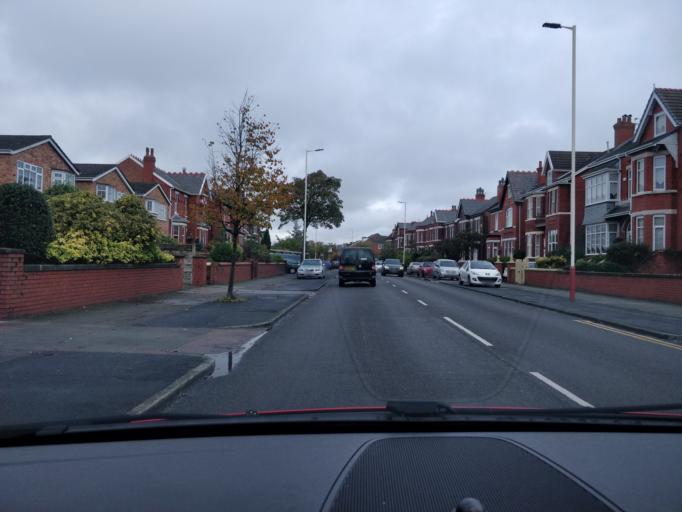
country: GB
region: England
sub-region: Sefton
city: Southport
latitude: 53.6255
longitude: -3.0124
